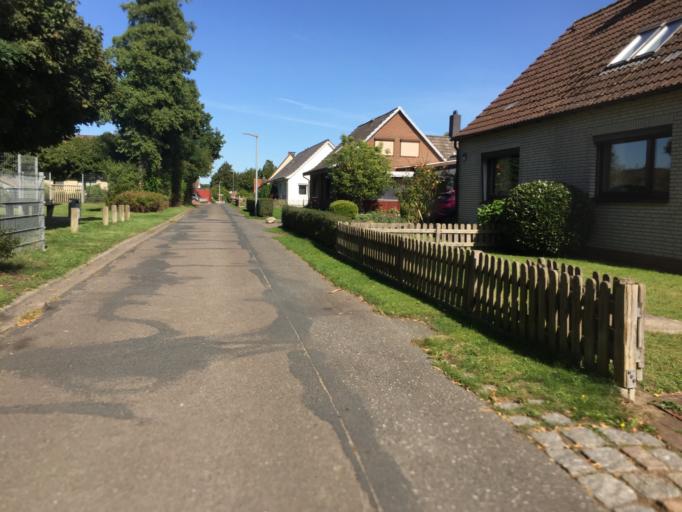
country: DE
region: Schleswig-Holstein
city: Itzehoe
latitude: 53.9095
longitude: 9.4950
